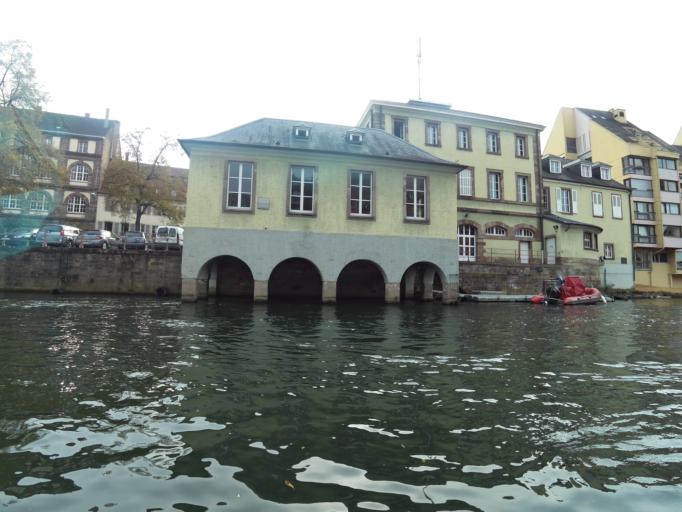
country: FR
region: Alsace
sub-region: Departement du Bas-Rhin
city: Strasbourg
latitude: 48.5792
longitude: 7.7442
